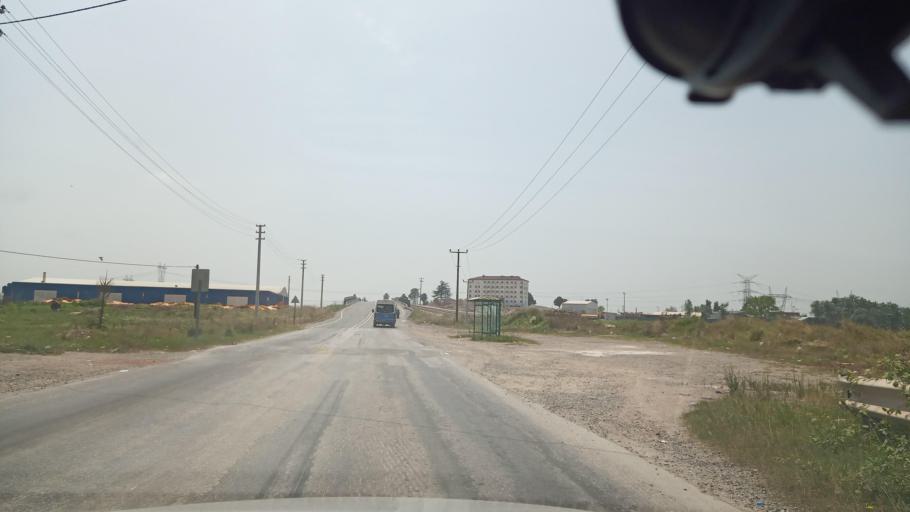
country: TR
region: Sakarya
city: Adapazari
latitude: 40.8271
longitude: 30.3966
